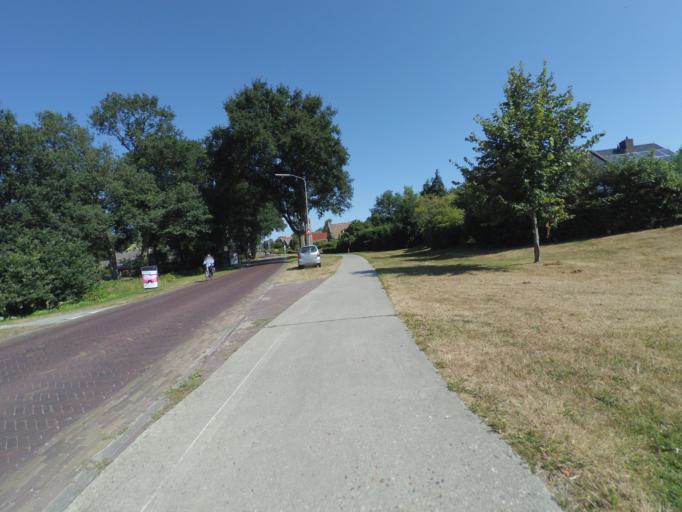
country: NL
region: Drenthe
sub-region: Gemeente Borger-Odoorn
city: Borger
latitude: 52.9157
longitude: 6.7965
